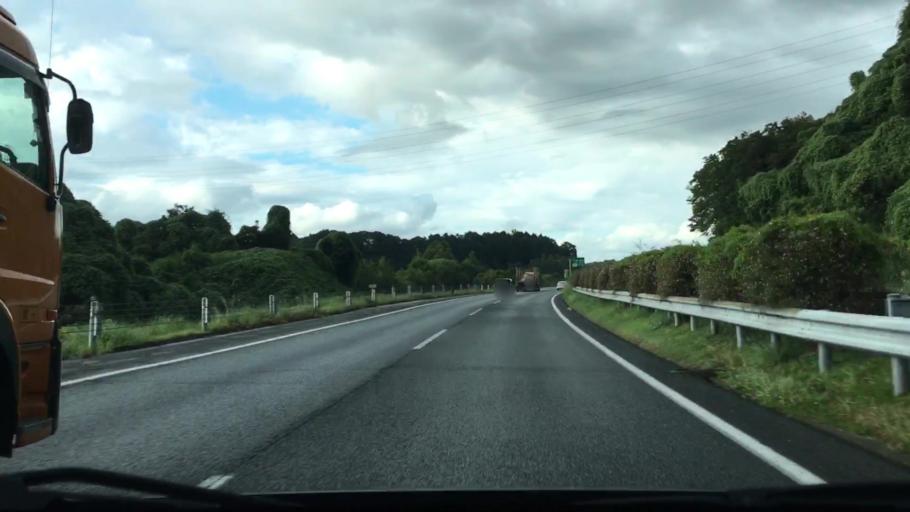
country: JP
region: Fukuoka
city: Koga
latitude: 33.7065
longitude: 130.4860
